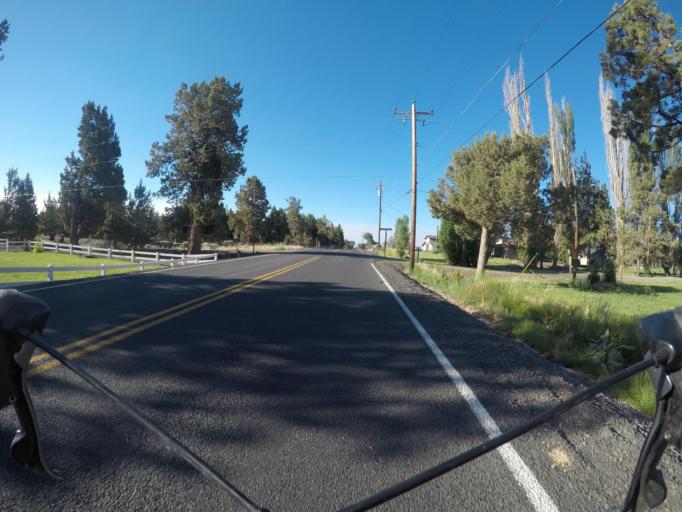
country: US
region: Oregon
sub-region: Deschutes County
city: Redmond
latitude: 44.2162
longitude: -121.2436
